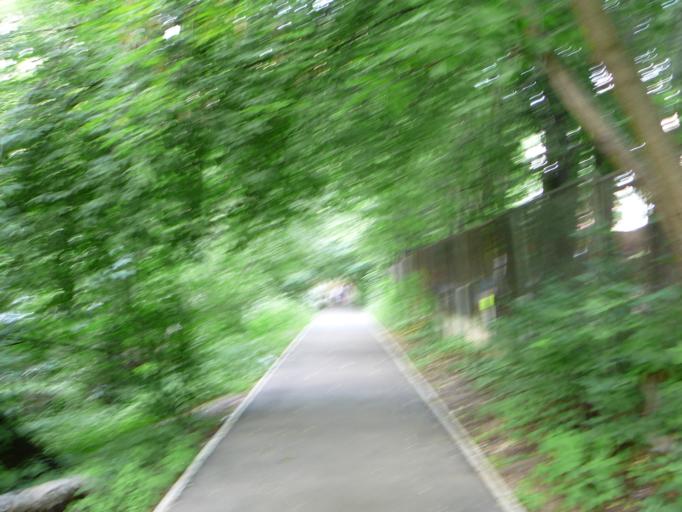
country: RU
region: Moskovskaya
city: Krasnogorsk
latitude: 55.8147
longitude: 37.3145
